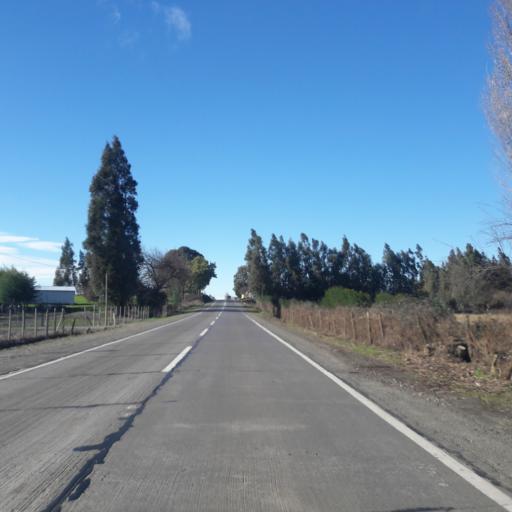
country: CL
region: Araucania
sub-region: Provincia de Malleco
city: Angol
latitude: -37.7653
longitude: -72.5616
